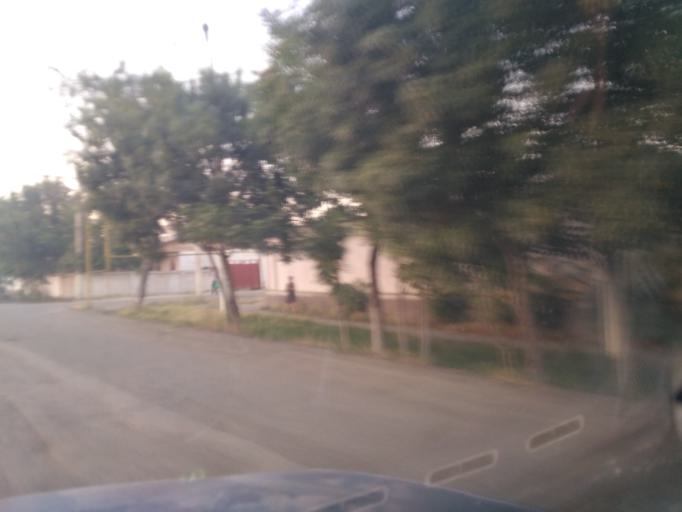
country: UZ
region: Sirdaryo
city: Guliston
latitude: 40.5034
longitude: 68.7688
